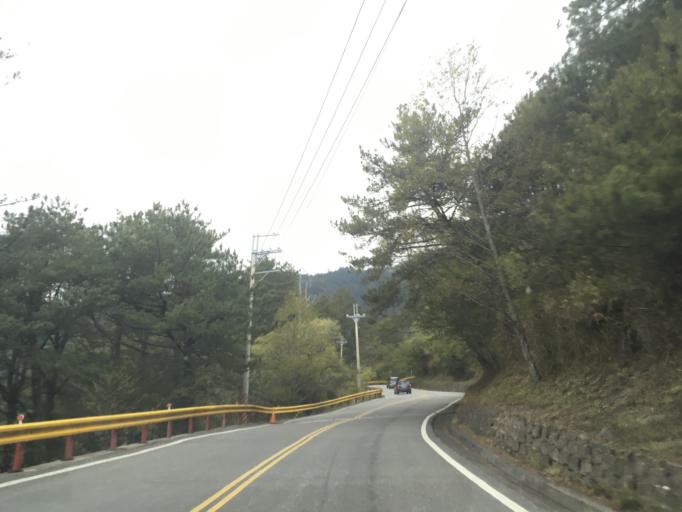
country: TW
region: Taiwan
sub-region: Hualien
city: Hualian
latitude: 24.1790
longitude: 121.3075
